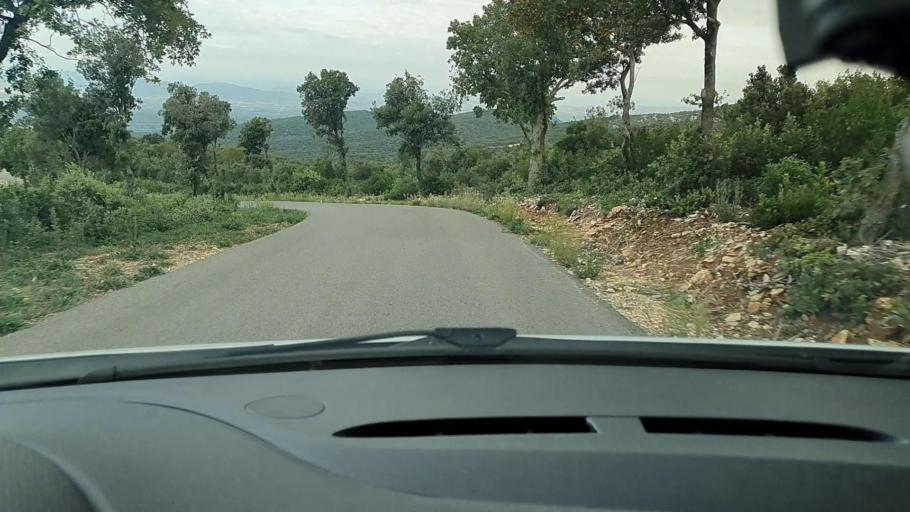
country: FR
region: Languedoc-Roussillon
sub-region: Departement du Gard
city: Mons
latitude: 44.1393
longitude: 4.2726
